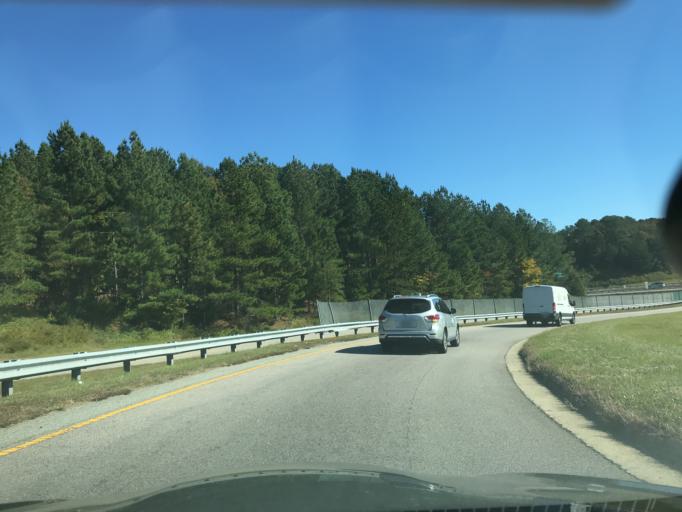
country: US
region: North Carolina
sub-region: Durham County
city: Durham
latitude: 36.0181
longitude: -78.9523
